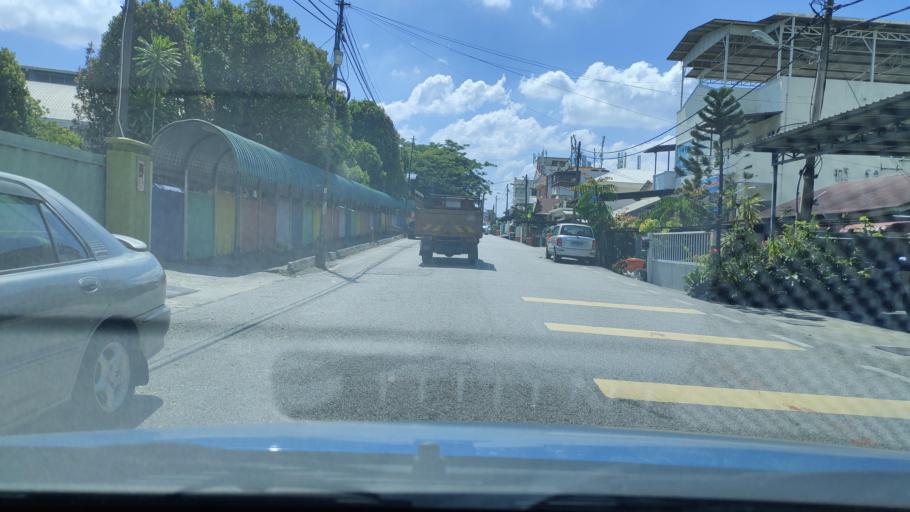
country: MY
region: Selangor
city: Kampong Baharu Balakong
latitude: 3.0250
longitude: 101.7016
